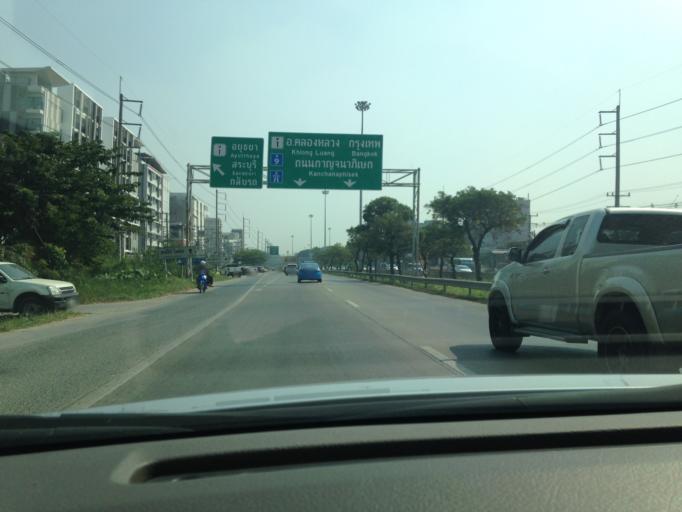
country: TH
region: Pathum Thani
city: Khlong Luang
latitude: 14.0653
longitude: 100.6106
